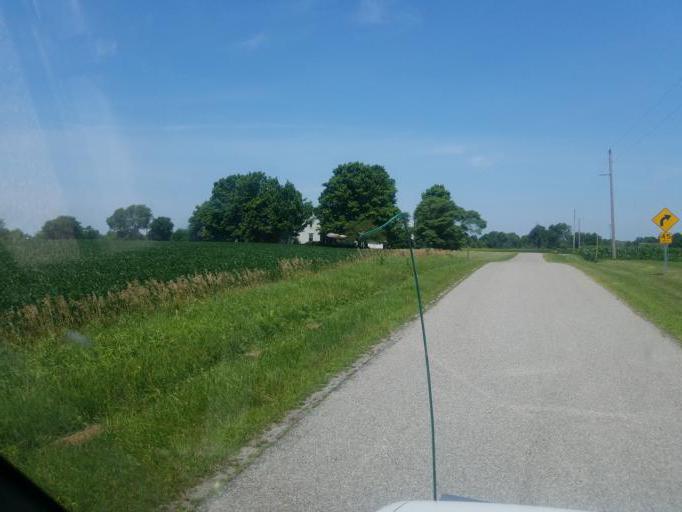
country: US
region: Ohio
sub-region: Logan County
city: West Liberty
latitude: 40.2841
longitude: -83.7703
